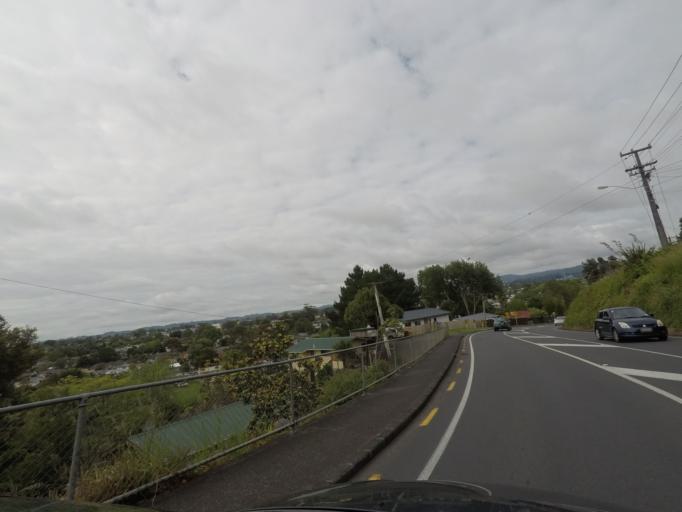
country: NZ
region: Auckland
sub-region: Auckland
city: Rosebank
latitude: -36.8562
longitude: 174.6111
